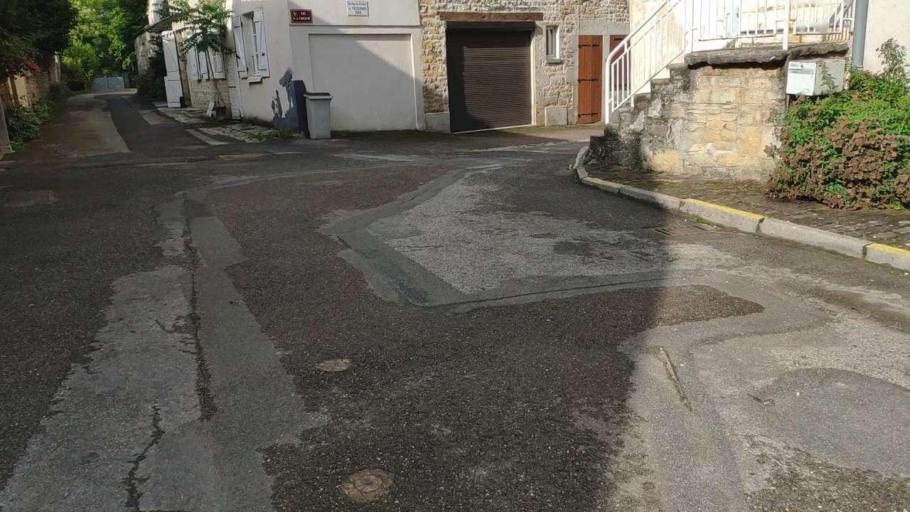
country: FR
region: Franche-Comte
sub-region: Departement du Jura
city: Poligny
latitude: 46.7982
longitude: 5.6179
